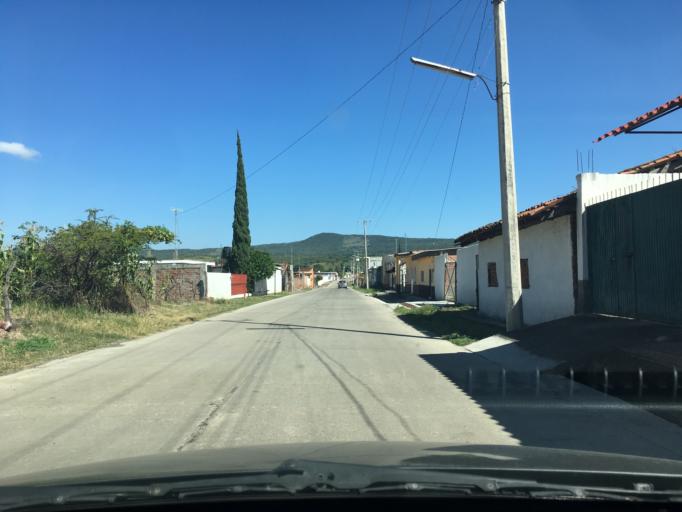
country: MX
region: Mexico
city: Tlazazalca
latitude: 19.9717
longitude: -102.1192
